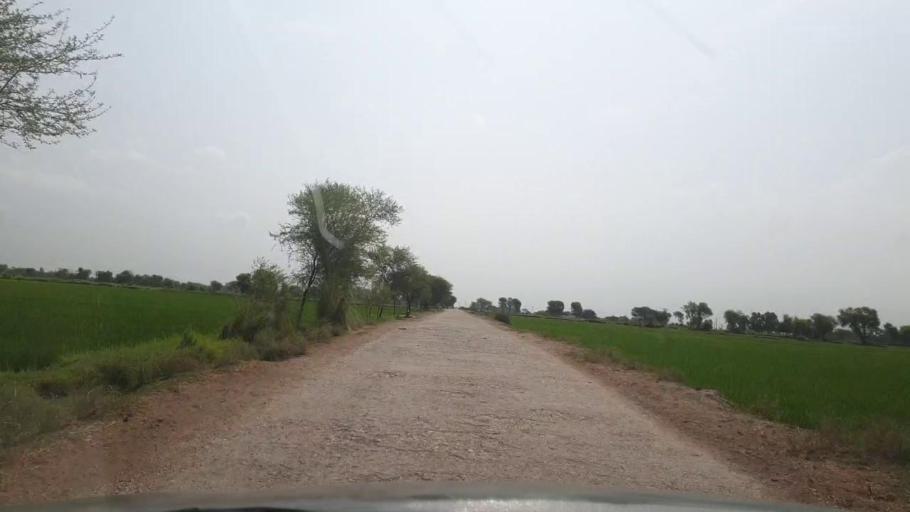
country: PK
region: Sindh
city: Ratodero
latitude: 27.8424
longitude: 68.3156
